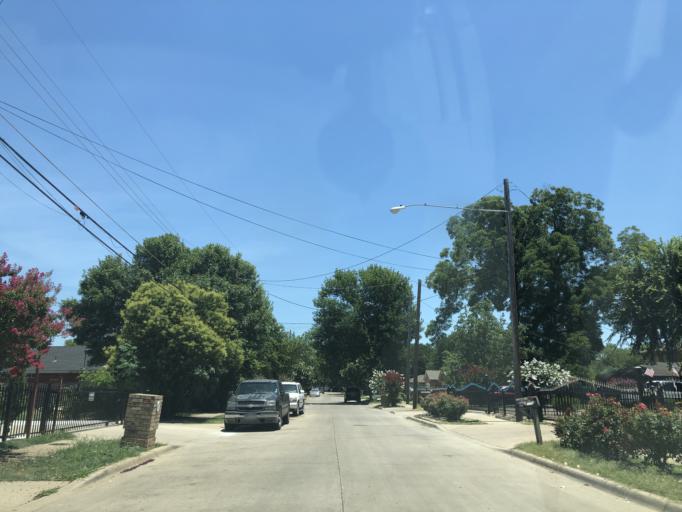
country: US
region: Texas
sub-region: Dallas County
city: Irving
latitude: 32.7950
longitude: -96.8997
